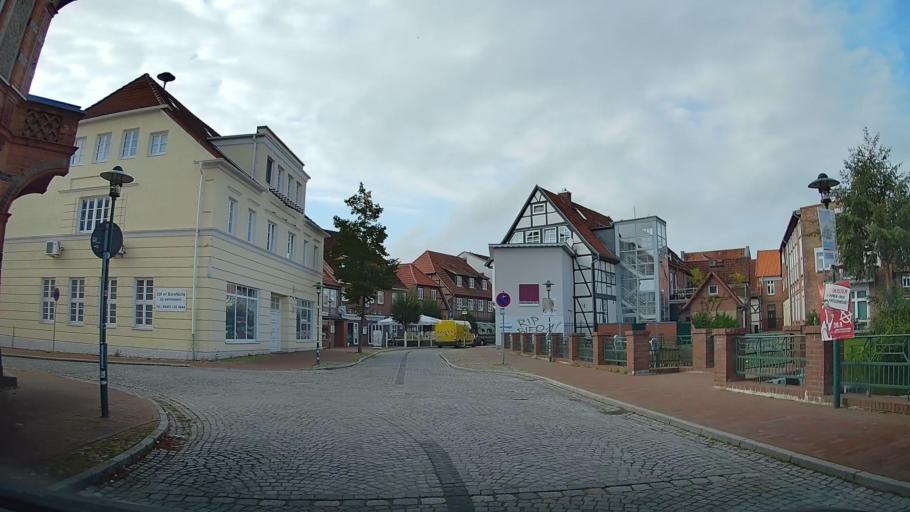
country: DE
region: Mecklenburg-Vorpommern
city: Hagenow
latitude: 53.4321
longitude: 11.1910
